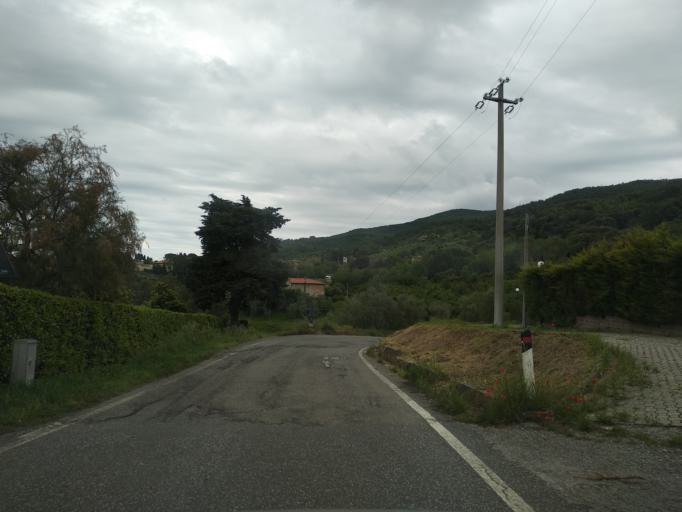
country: IT
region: Tuscany
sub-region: Provincia di Livorno
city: Collesalvetti
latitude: 43.5414
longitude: 10.4401
